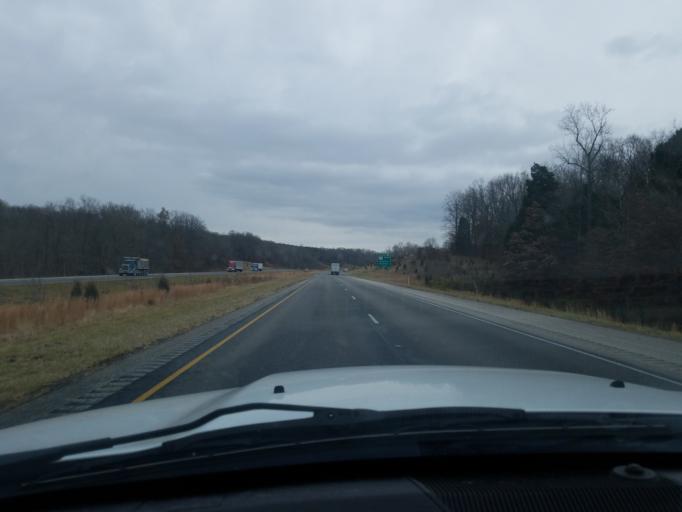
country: US
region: Indiana
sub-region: Crawford County
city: English
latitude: 38.2345
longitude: -86.4945
